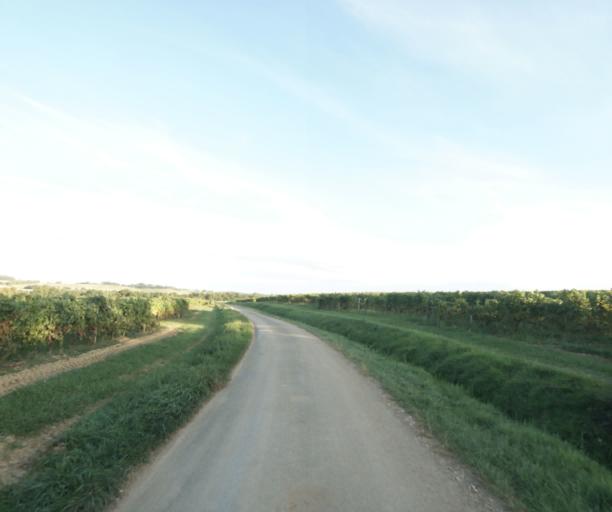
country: FR
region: Midi-Pyrenees
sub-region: Departement du Gers
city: Gondrin
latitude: 43.8615
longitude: 0.2978
